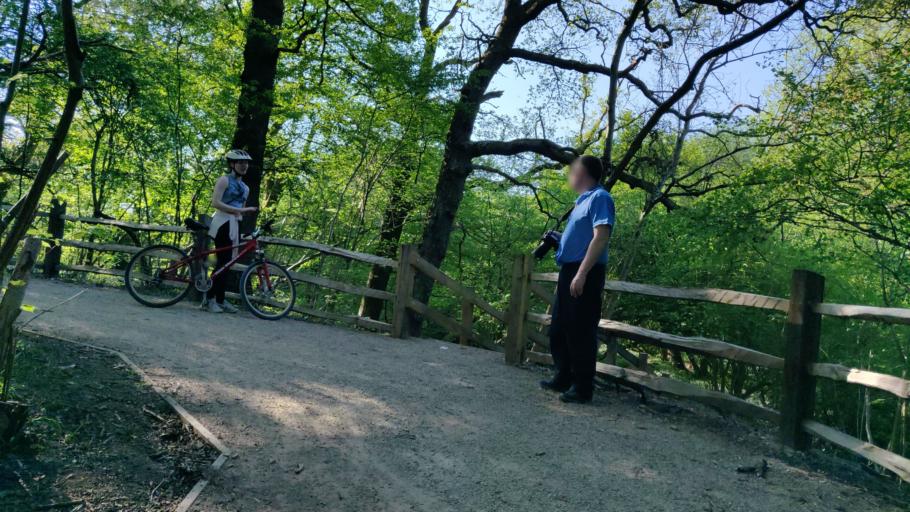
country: GB
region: England
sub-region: West Sussex
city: Southwater
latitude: 51.0518
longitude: -0.3631
